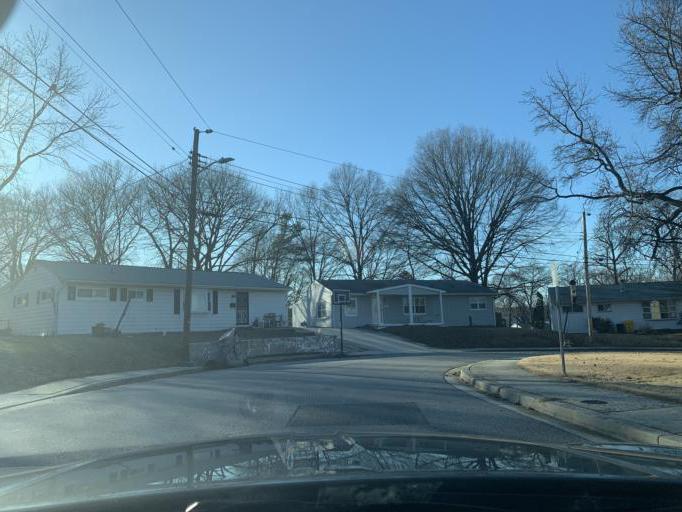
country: US
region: Maryland
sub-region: Anne Arundel County
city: Glen Burnie
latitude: 39.1481
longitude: -76.6269
